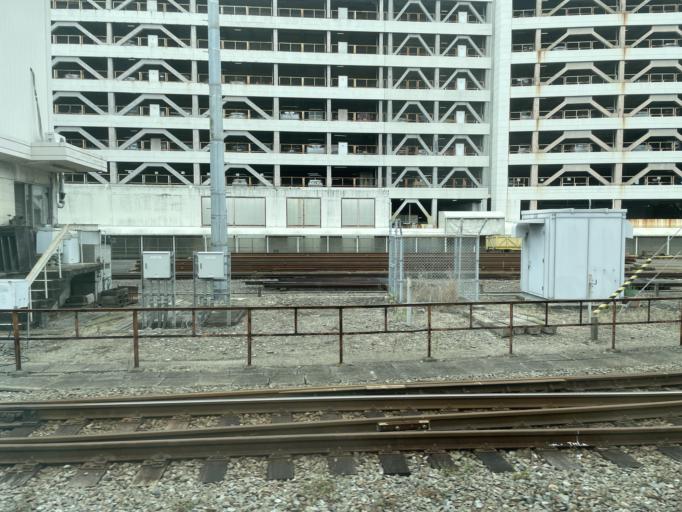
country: JP
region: Wakayama
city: Wakayama-shi
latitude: 34.2339
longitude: 135.1909
